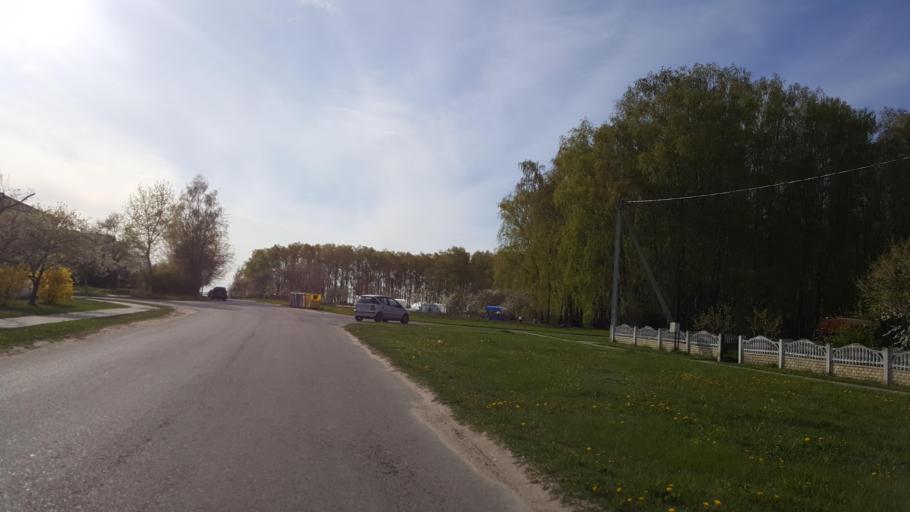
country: BY
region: Brest
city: Vysokaye
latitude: 52.4064
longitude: 23.4605
